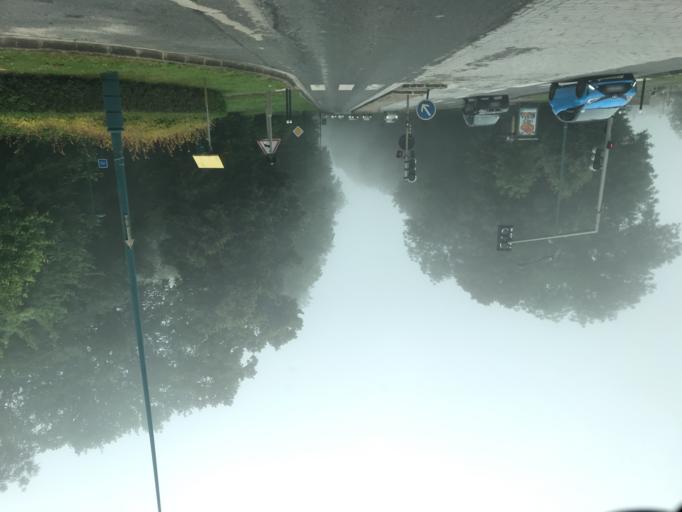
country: FR
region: Ile-de-France
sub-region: Departement de Seine-et-Marne
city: Montevrain
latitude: 48.8782
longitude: 2.7557
